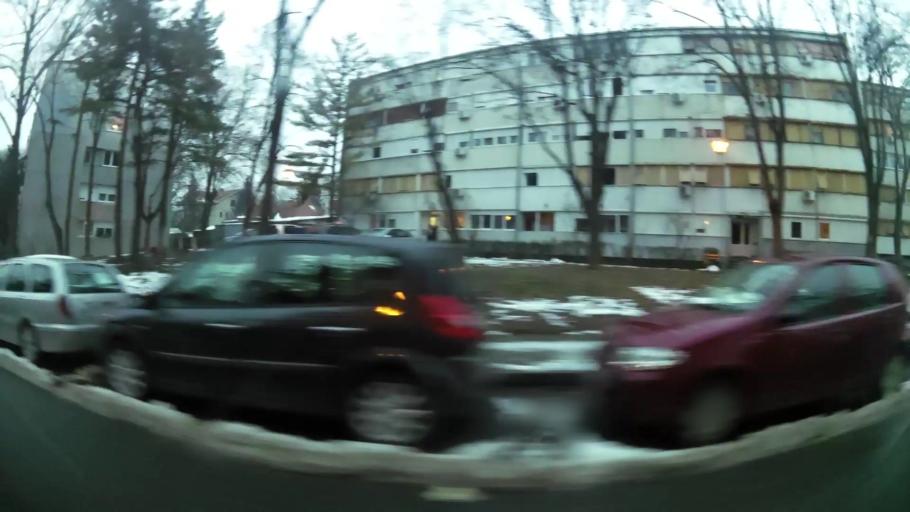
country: RS
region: Central Serbia
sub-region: Belgrade
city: Vozdovac
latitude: 44.7713
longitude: 20.4894
